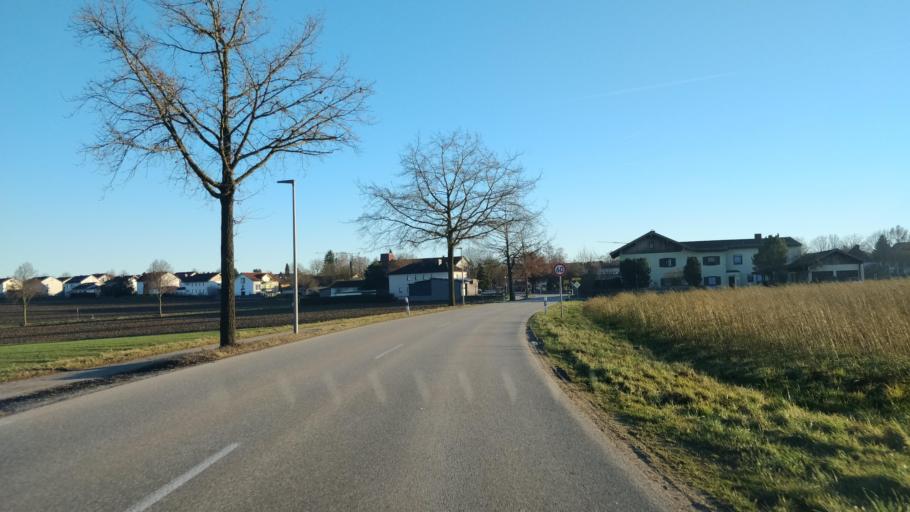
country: DE
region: Bavaria
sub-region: Upper Bavaria
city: Obertaufkirchen
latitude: 48.2654
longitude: 12.2751
